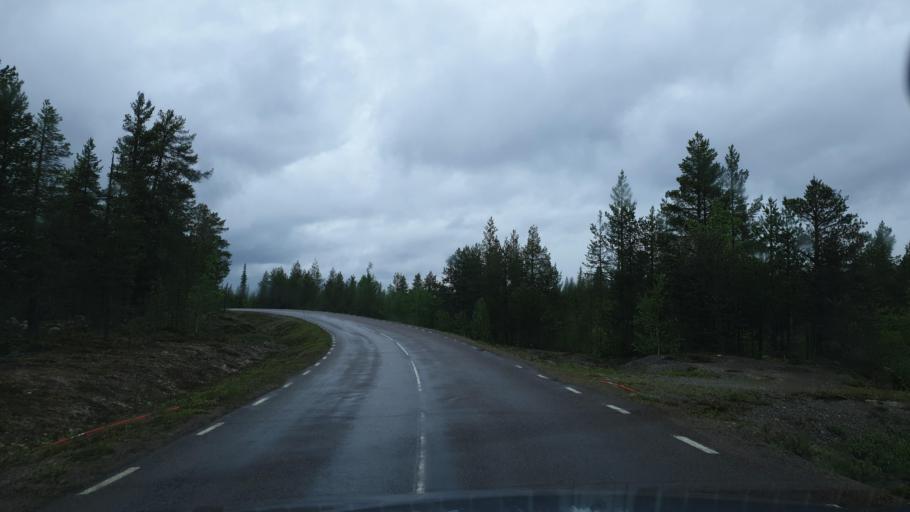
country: SE
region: Norrbotten
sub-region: Kiruna Kommun
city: Kiruna
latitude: 67.8729
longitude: 20.9885
